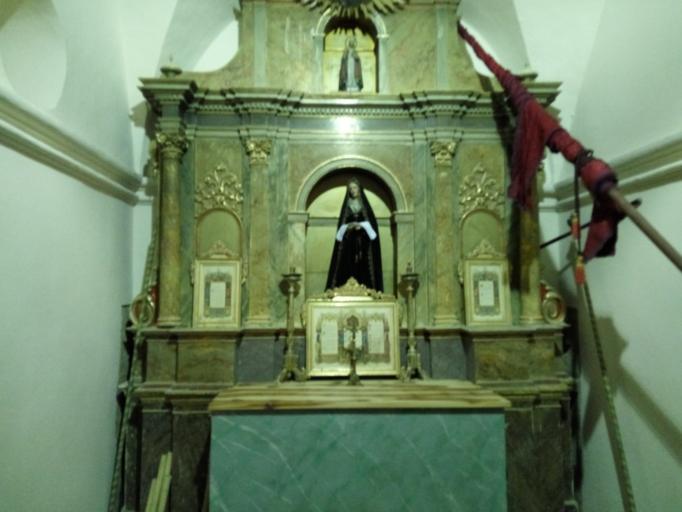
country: ES
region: Catalonia
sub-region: Provincia de Barcelona
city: Capolat
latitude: 42.0449
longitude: 1.7829
